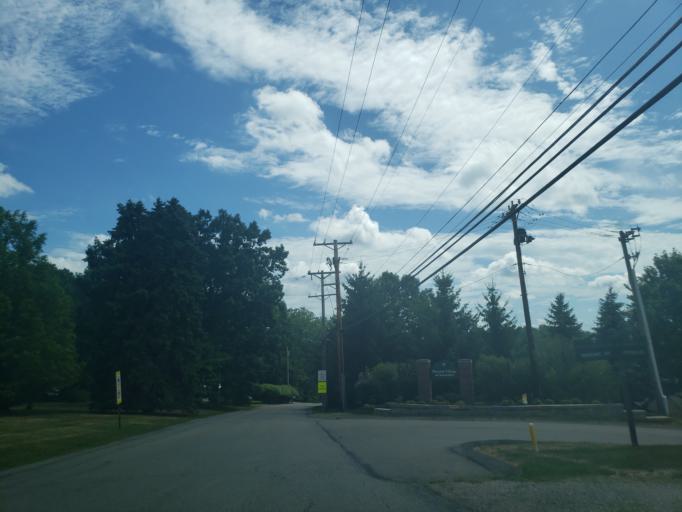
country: US
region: Pennsylvania
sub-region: Allegheny County
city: Coraopolis
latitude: 40.5276
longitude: -80.1405
